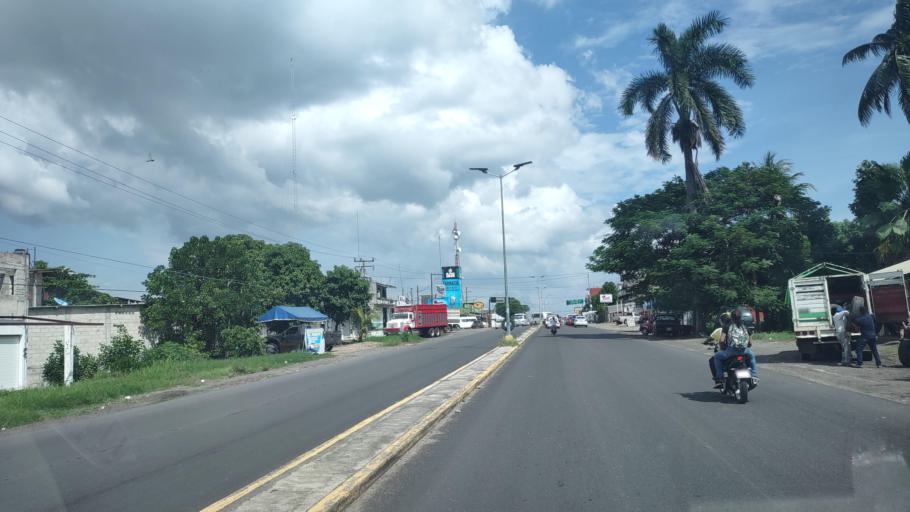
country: MX
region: Veracruz
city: Martinez de la Torre
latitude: 20.0726
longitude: -97.0660
